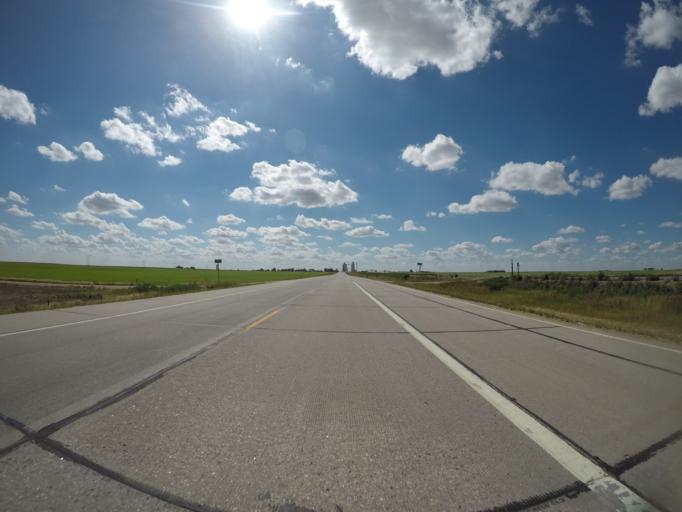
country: US
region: Colorado
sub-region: Phillips County
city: Holyoke
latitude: 40.6099
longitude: -102.4555
